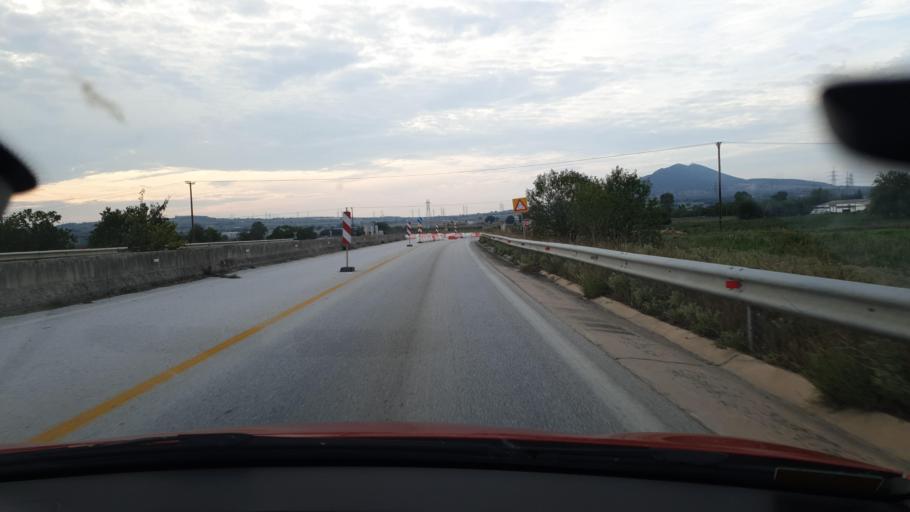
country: GR
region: Central Macedonia
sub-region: Nomos Thessalonikis
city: Assiros
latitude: 40.7850
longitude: 23.0110
